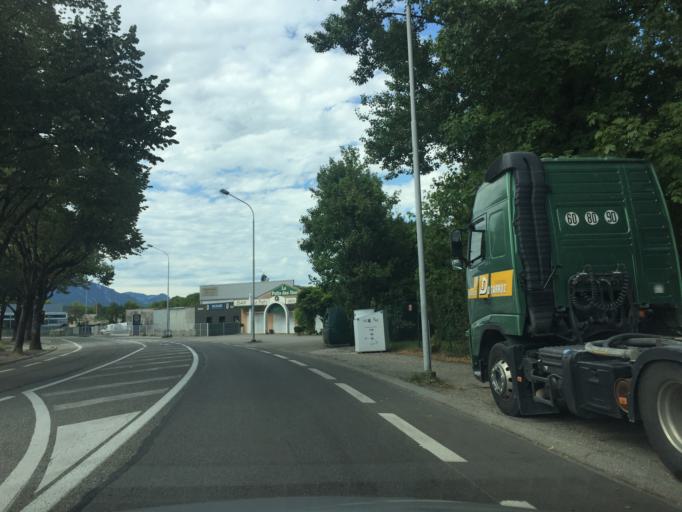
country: FR
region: Rhone-Alpes
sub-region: Departement de la Savoie
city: Cognin
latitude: 45.5821
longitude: 5.9030
